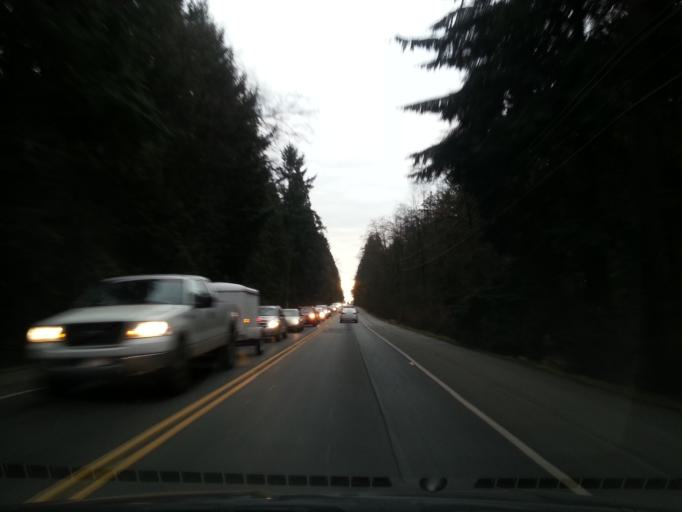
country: CA
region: British Columbia
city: Surrey
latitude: 49.1736
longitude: -122.8211
